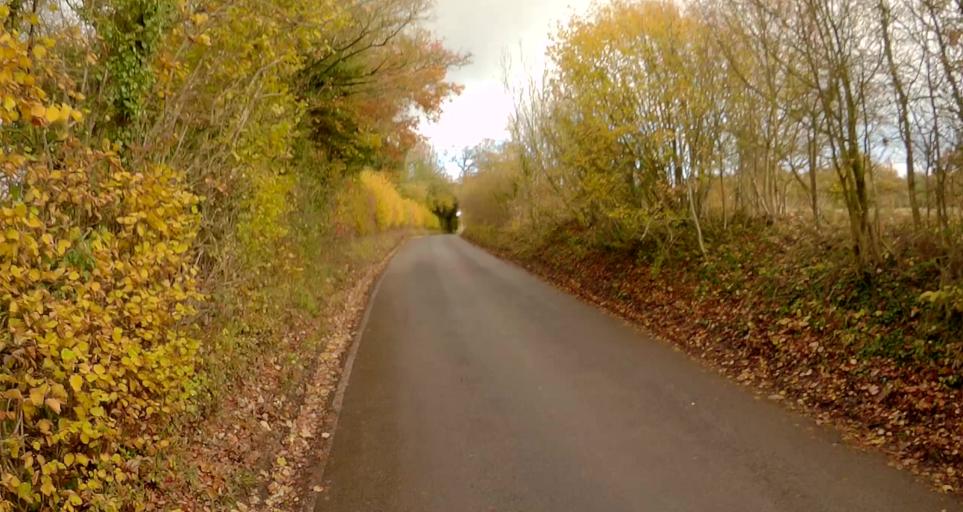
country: GB
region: England
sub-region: Hampshire
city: Old Basing
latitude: 51.2325
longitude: -1.0275
